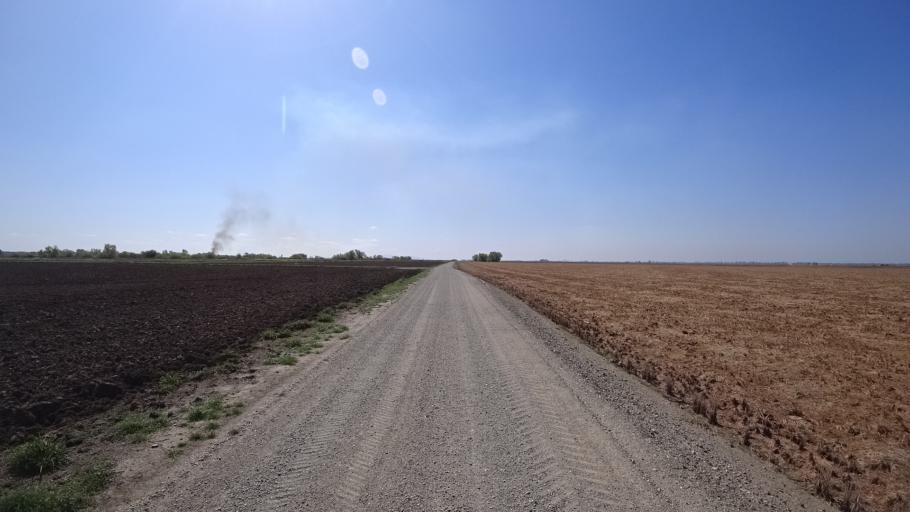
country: US
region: California
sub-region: Butte County
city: Durham
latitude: 39.5368
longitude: -121.9083
